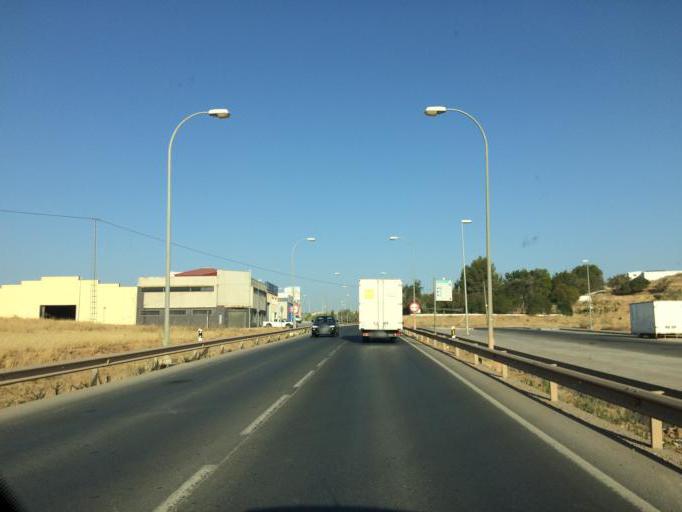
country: ES
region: Andalusia
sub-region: Provincia de Malaga
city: Campillos
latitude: 37.0520
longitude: -4.8676
